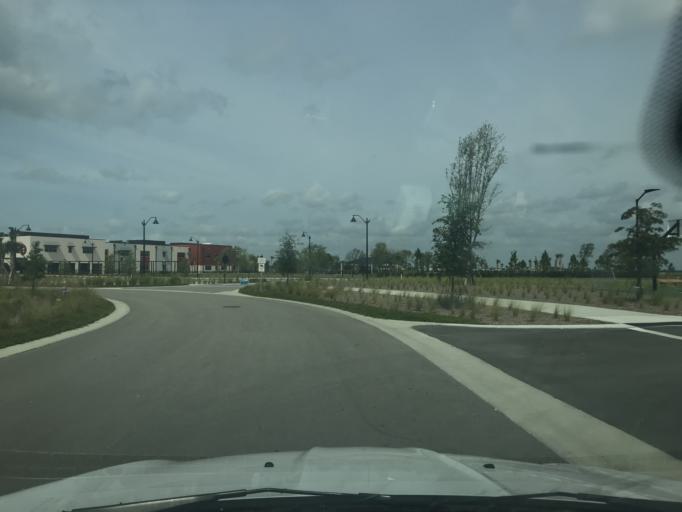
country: US
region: Florida
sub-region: Lee County
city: Olga
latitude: 26.7830
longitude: -81.7384
